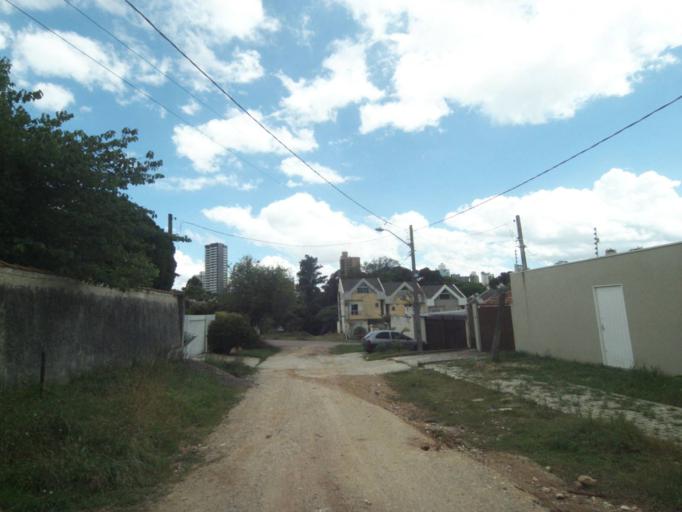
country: BR
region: Parana
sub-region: Curitiba
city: Curitiba
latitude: -25.4320
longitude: -49.3284
